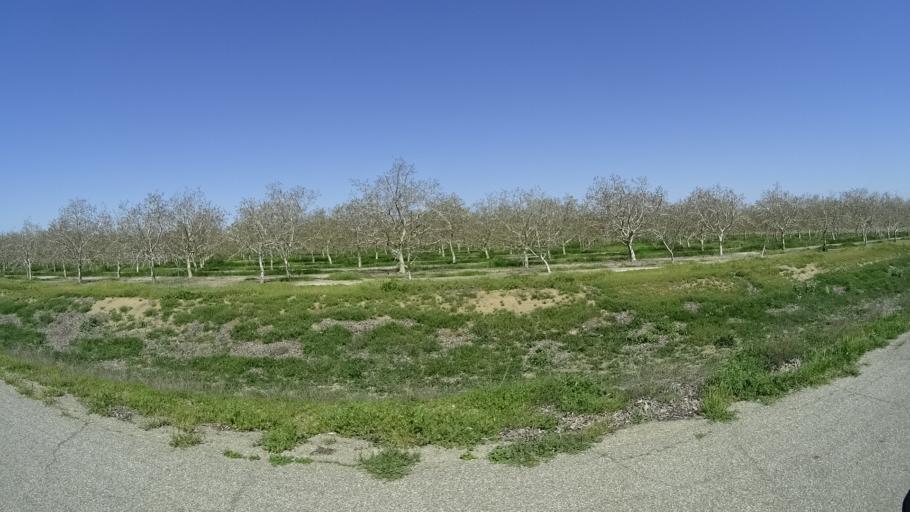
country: US
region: California
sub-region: Colusa County
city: Colusa
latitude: 39.4434
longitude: -121.9691
